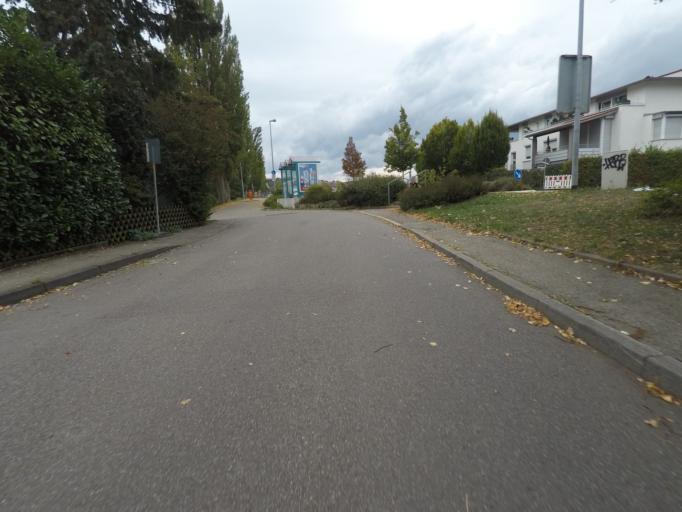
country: DE
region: Baden-Wuerttemberg
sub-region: Regierungsbezirk Stuttgart
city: Filderstadt
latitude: 48.6549
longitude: 9.2107
